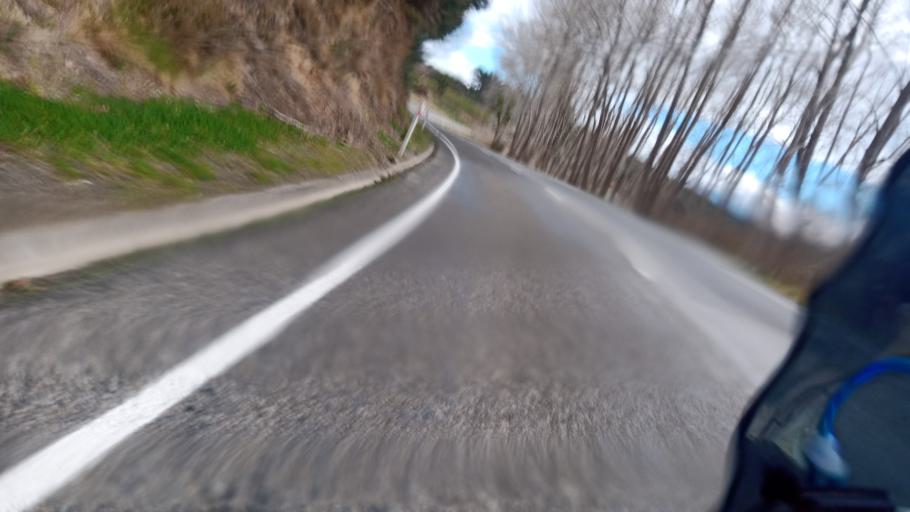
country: NZ
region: Gisborne
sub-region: Gisborne District
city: Gisborne
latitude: -38.0273
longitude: 178.2753
